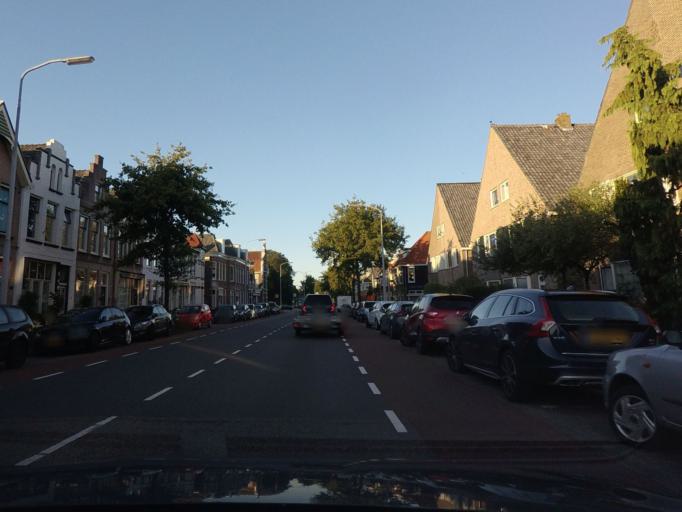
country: NL
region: North Holland
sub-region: Gemeente Alkmaar
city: Alkmaar
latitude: 52.6221
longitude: 4.7357
